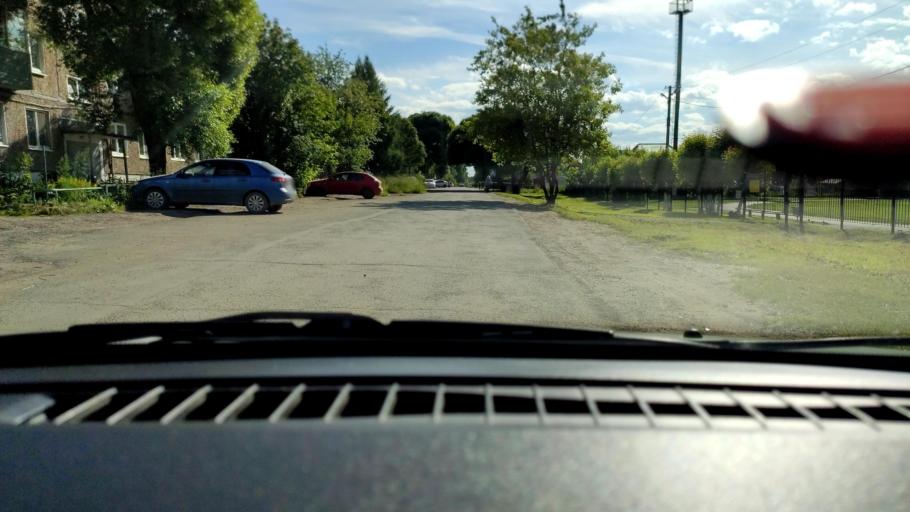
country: RU
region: Perm
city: Kultayevo
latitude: 57.8998
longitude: 55.9365
